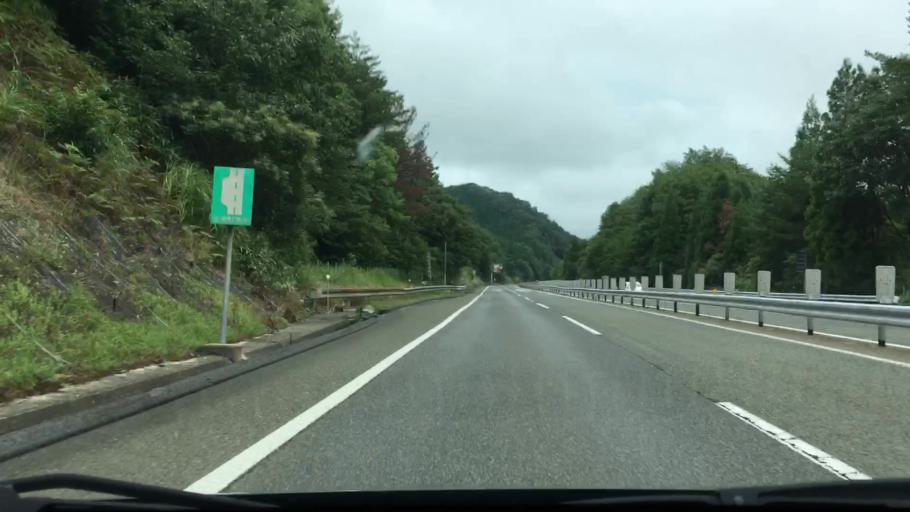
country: JP
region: Hiroshima
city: Shobara
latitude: 34.8723
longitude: 133.1185
